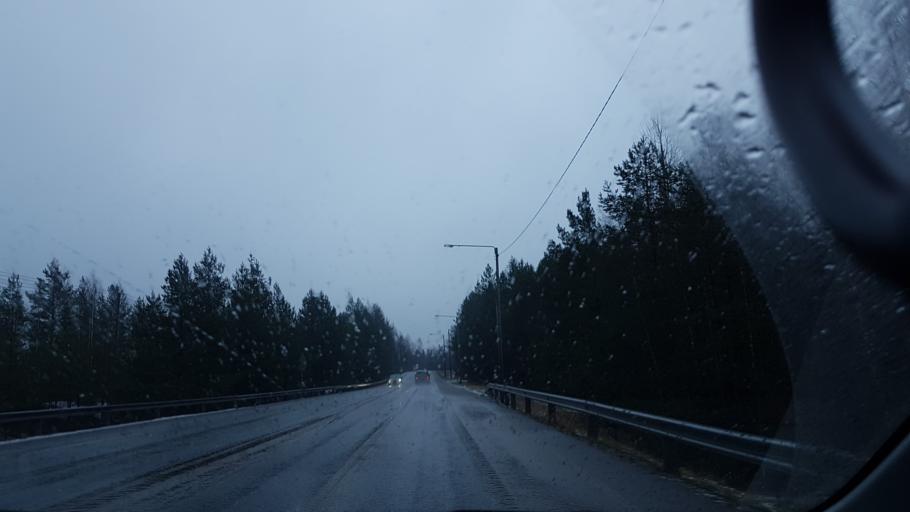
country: FI
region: Uusimaa
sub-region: Helsinki
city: Tuusula
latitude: 60.3639
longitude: 25.0099
